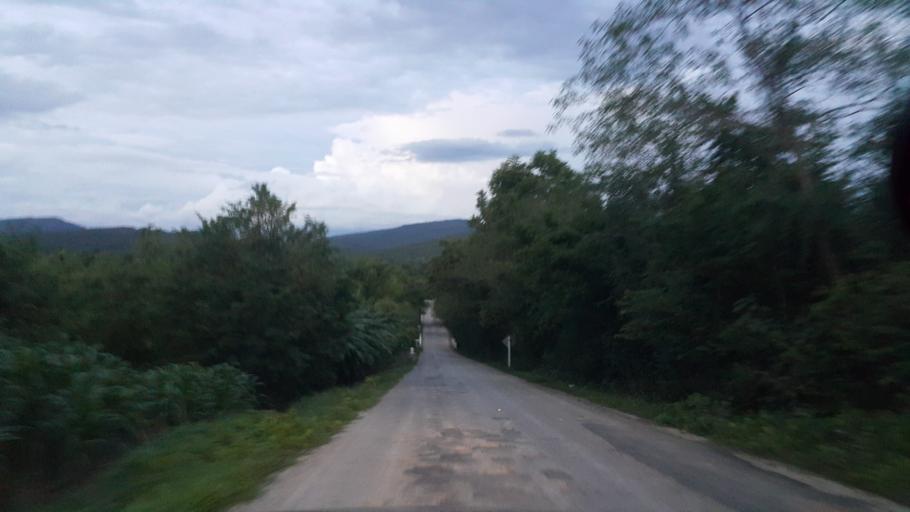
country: TH
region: Loei
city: Phu Ruea
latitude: 17.5307
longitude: 101.2233
